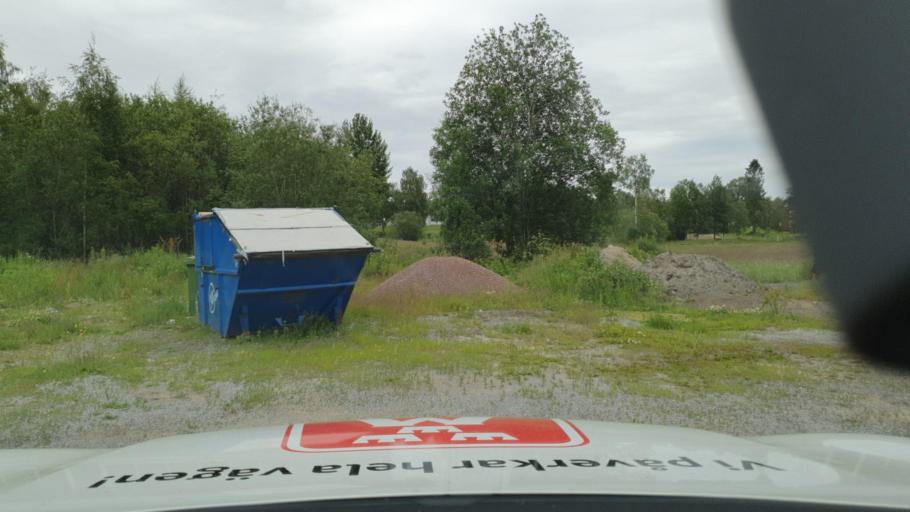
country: SE
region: Vaesterbotten
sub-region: Nordmalings Kommun
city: Nordmaling
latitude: 63.5707
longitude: 19.5258
